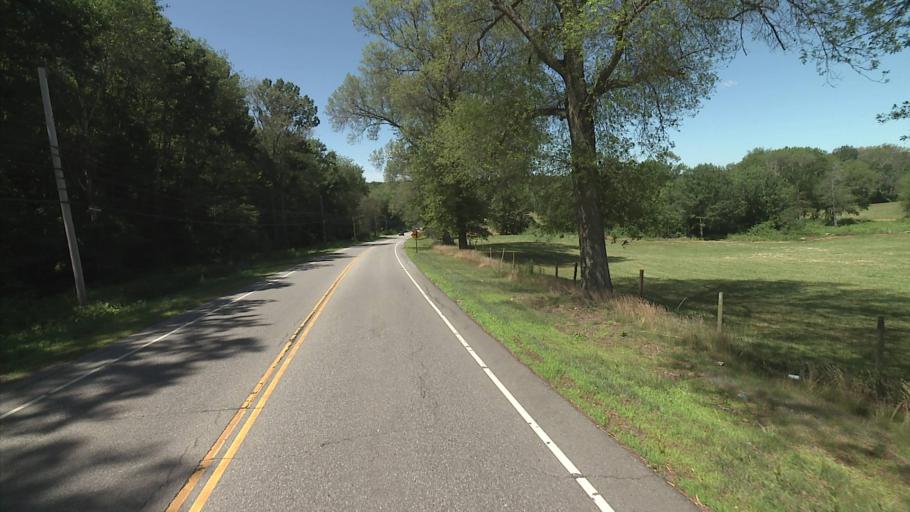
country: US
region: Connecticut
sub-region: New London County
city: Colchester
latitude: 41.5605
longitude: -72.3617
